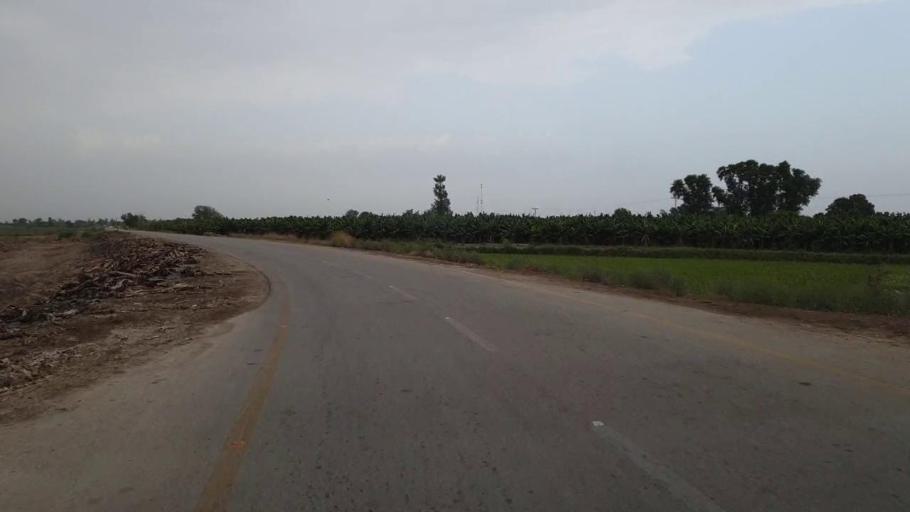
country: PK
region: Sindh
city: Bandhi
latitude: 26.5809
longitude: 68.2810
